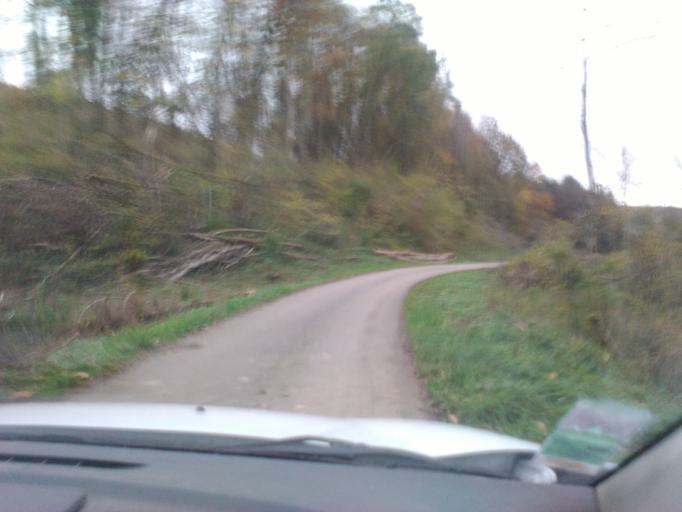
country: FR
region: Lorraine
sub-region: Departement des Vosges
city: Mirecourt
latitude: 48.2789
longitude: 6.2171
